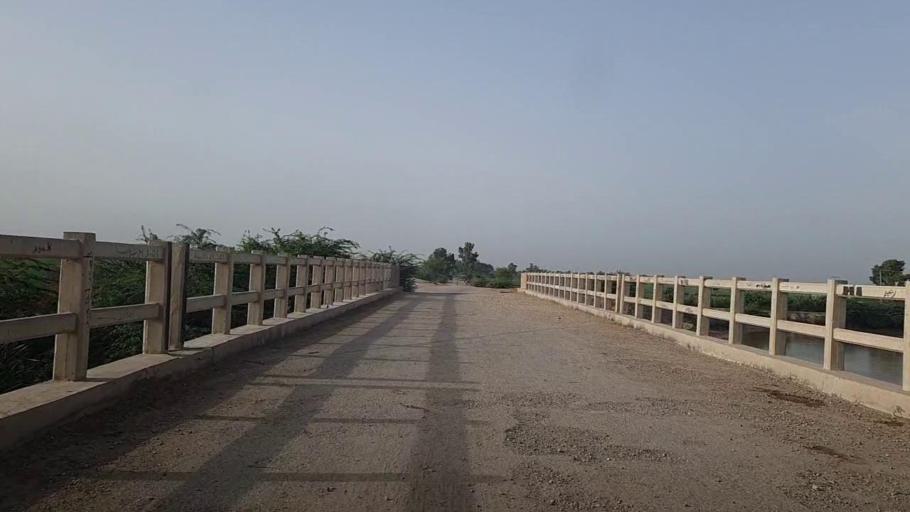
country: PK
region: Sindh
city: Mehar
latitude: 27.1280
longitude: 67.7891
